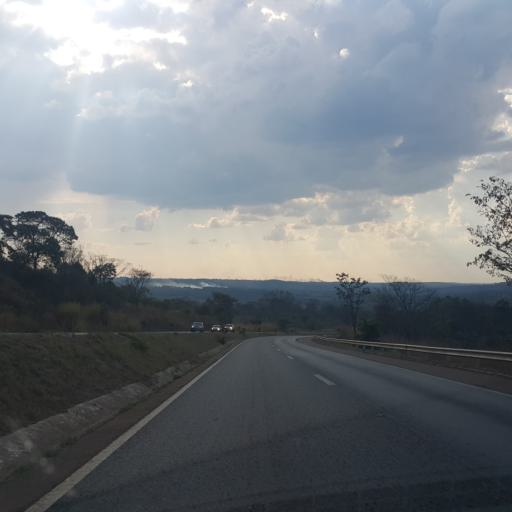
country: BR
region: Goias
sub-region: Abadiania
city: Abadiania
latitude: -16.1099
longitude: -48.4464
